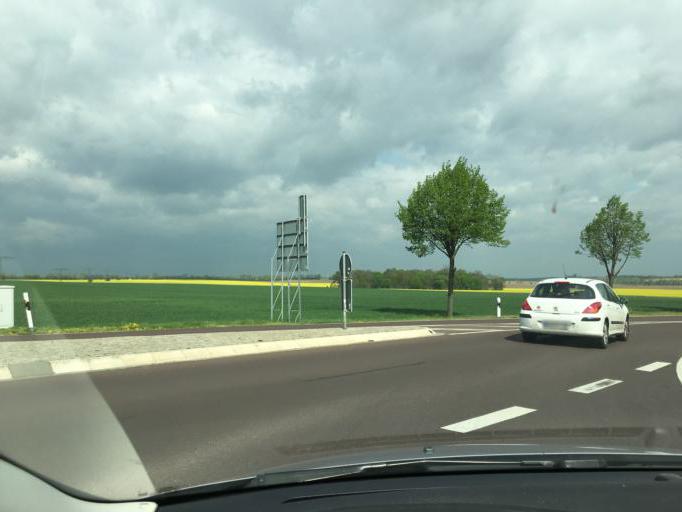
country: DE
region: Saxony-Anhalt
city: Giersleben
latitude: 51.7225
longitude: 11.5844
